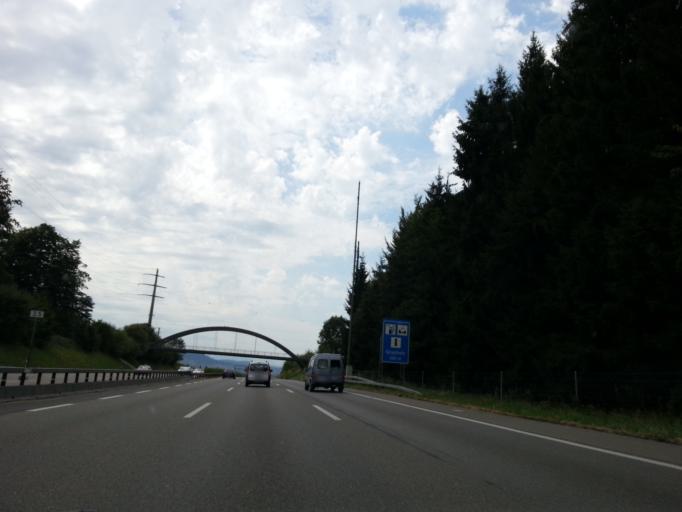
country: CH
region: Bern
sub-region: Bern-Mittelland District
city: Bolligen
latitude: 46.9956
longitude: 7.4846
